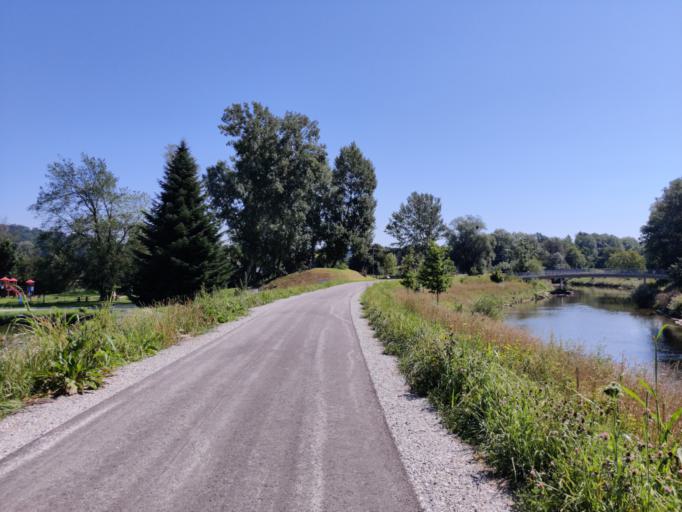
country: AT
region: Styria
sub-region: Politischer Bezirk Leibnitz
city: Wildon
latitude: 46.8880
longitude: 15.5076
